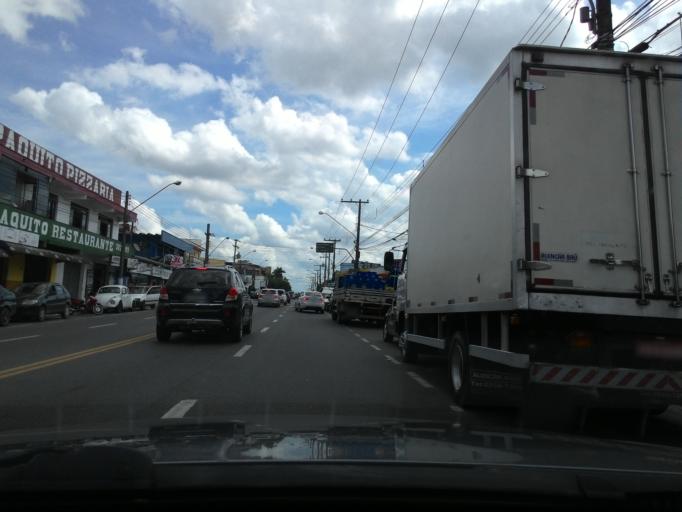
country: BR
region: Sao Paulo
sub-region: Registro
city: Registro
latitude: -24.4981
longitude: -47.8503
